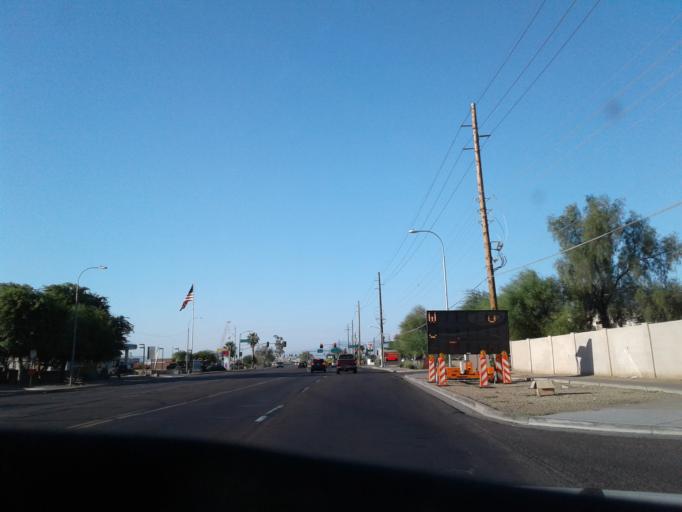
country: US
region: Arizona
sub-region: Maricopa County
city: Glendale
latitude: 33.4677
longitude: -112.1865
